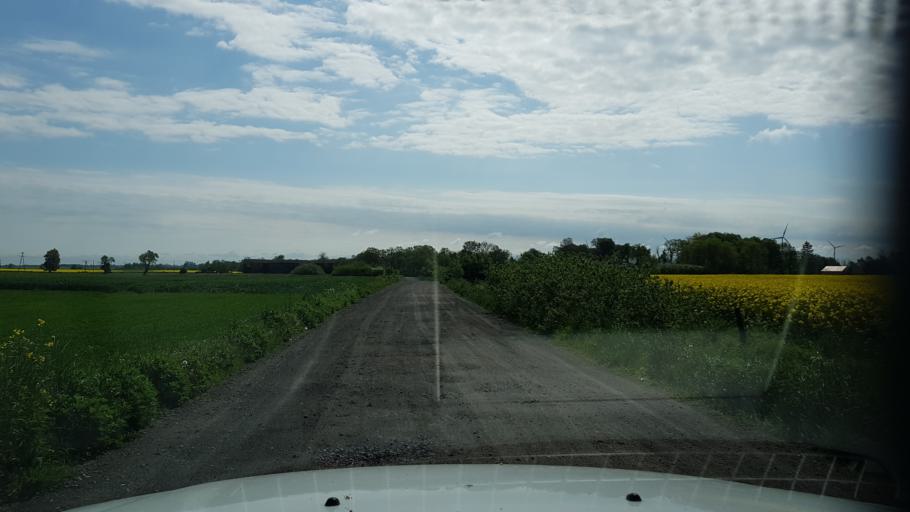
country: PL
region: West Pomeranian Voivodeship
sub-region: Powiat kolobrzeski
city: Ustronie Morskie
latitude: 54.2148
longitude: 15.8411
